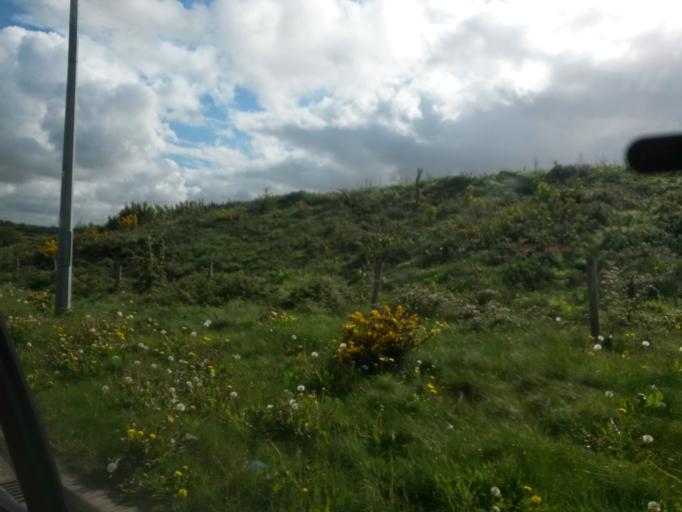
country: IE
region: Leinster
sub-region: Loch Garman
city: Enniscorthy
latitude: 52.5439
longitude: -6.5500
